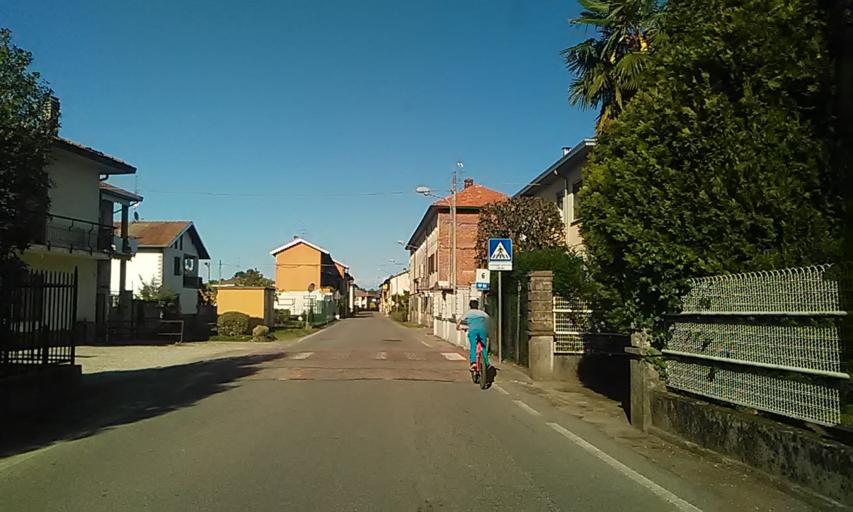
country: IT
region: Piedmont
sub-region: Provincia di Novara
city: Cavaglio D'Agogna
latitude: 45.6112
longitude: 8.4864
